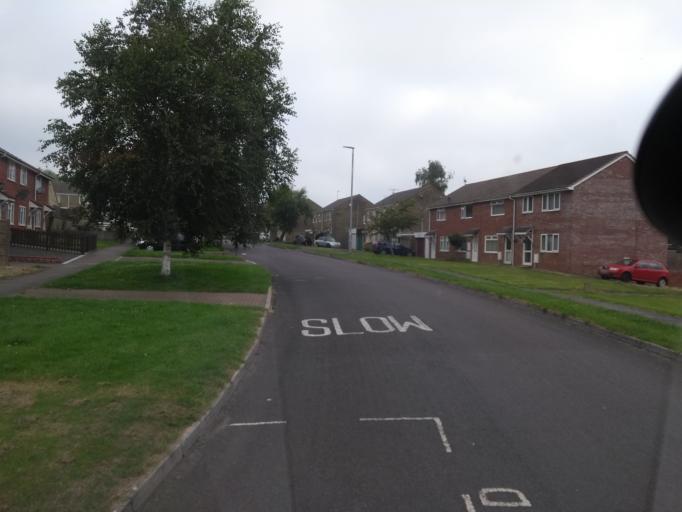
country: GB
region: England
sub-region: Somerset
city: Chard
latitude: 50.8800
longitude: -2.9606
